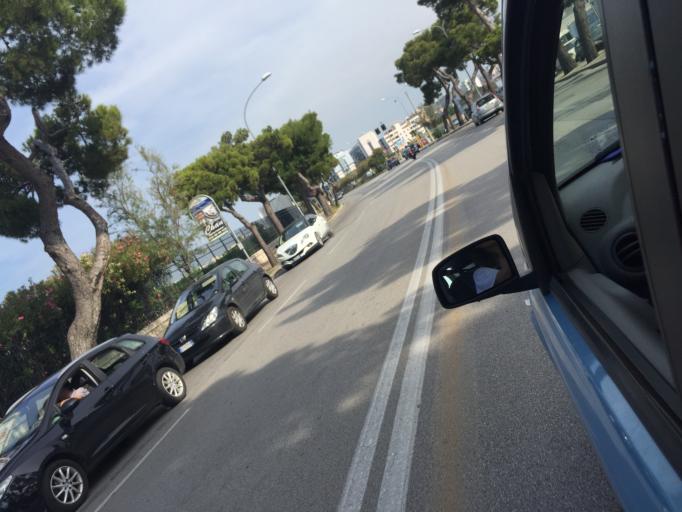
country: IT
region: Apulia
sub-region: Provincia di Bari
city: Bari
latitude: 41.1336
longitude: 16.8445
